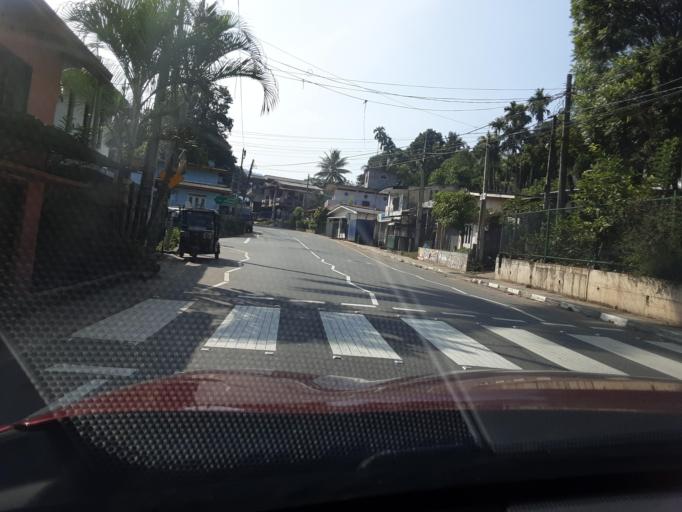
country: LK
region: Uva
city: Badulla
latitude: 6.9787
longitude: 81.0833
